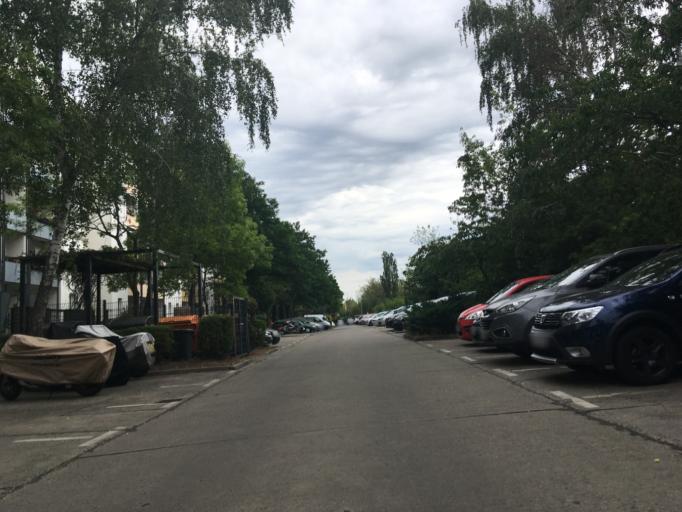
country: DE
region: Berlin
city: Wartenberg
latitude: 52.5768
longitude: 13.5115
